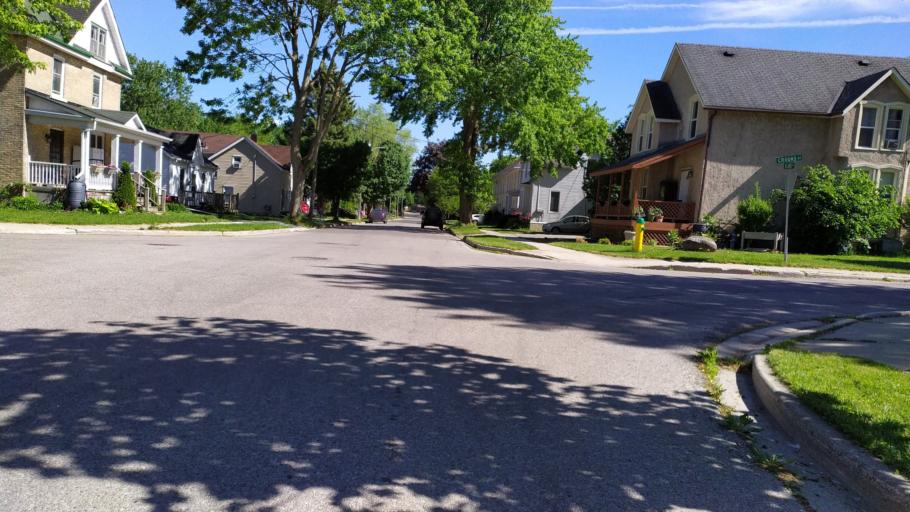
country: CA
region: Ontario
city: Stratford
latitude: 43.3608
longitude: -80.9836
